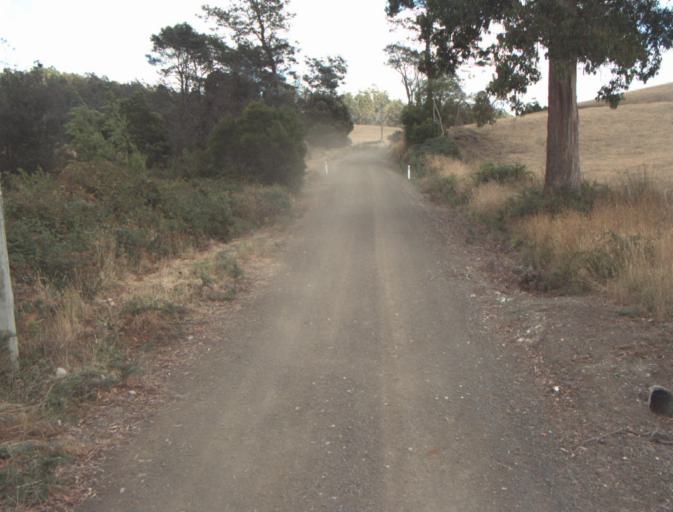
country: AU
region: Tasmania
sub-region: Launceston
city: Mayfield
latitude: -41.1990
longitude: 147.2271
